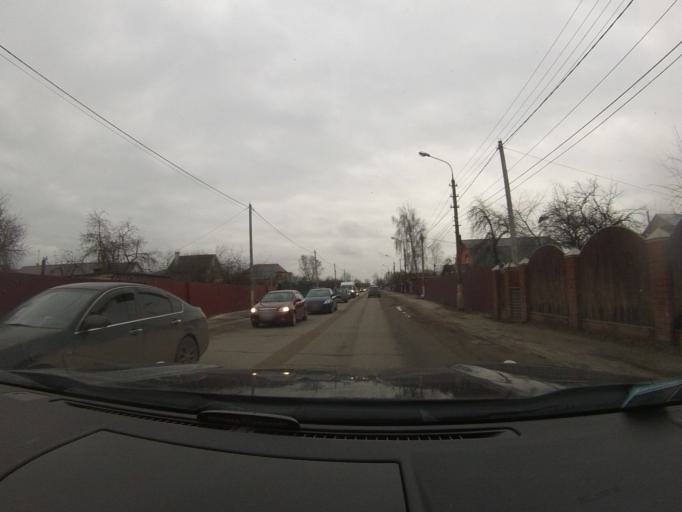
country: RU
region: Moskovskaya
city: Lopatinskiy
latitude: 55.3299
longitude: 38.7119
